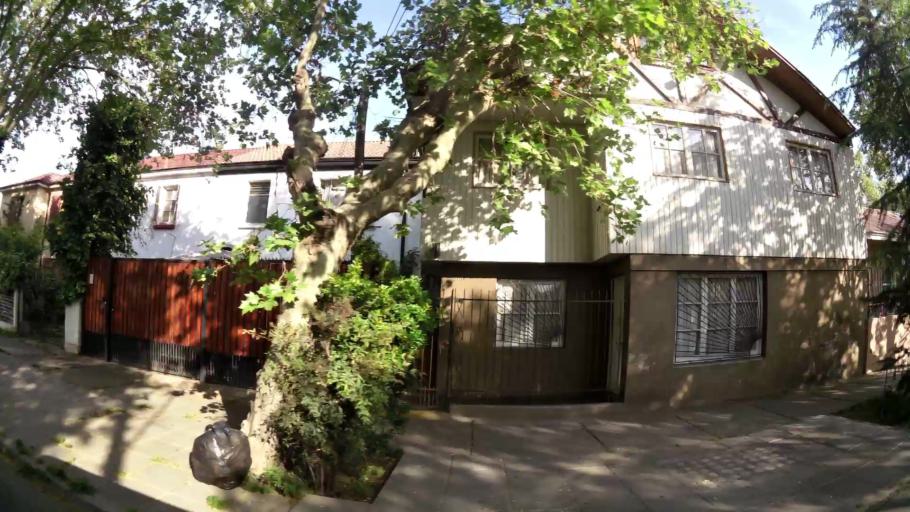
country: CL
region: Santiago Metropolitan
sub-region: Provincia de Santiago
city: Santiago
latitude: -33.5083
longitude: -70.6656
